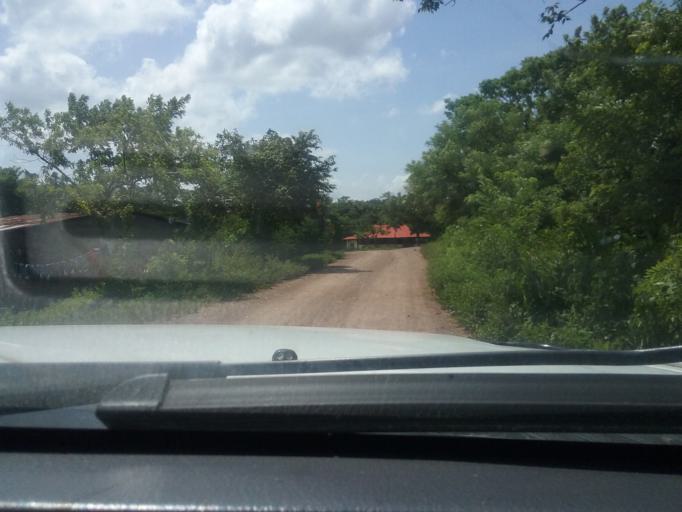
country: NI
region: Matagalpa
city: Terrabona
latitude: 12.6829
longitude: -85.9551
